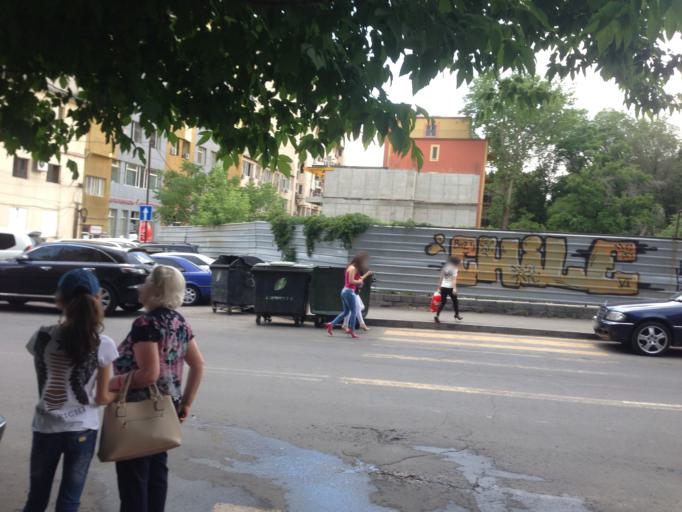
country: AM
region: Yerevan
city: Yerevan
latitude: 40.1742
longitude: 44.5104
